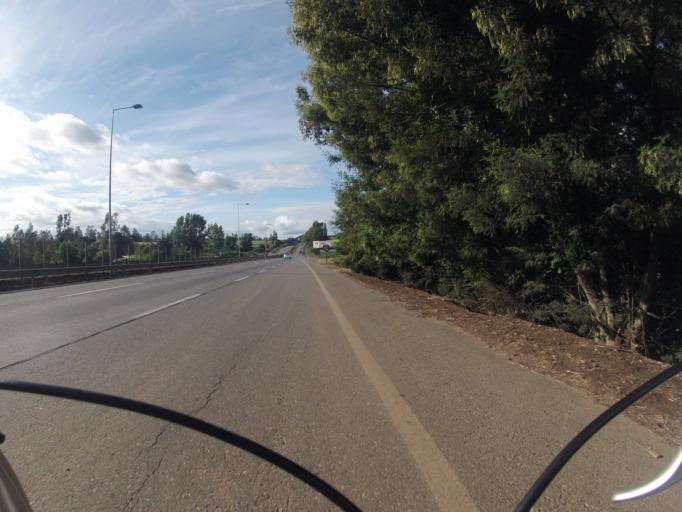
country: CL
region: Araucania
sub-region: Provincia de Cautin
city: Temuco
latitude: -38.8179
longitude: -72.6236
